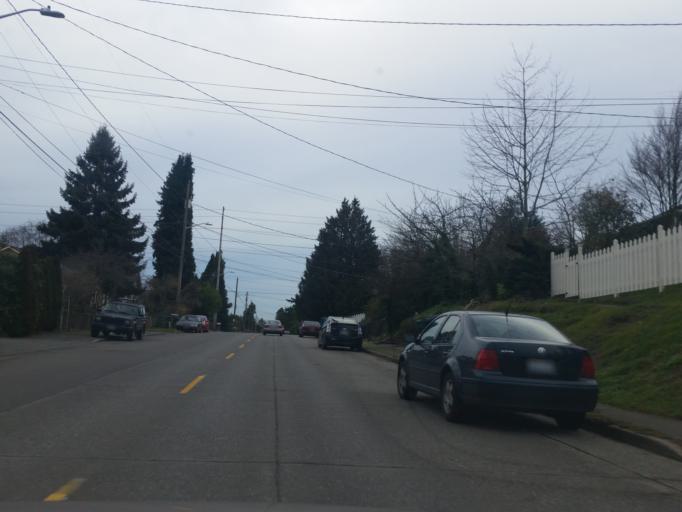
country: US
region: Washington
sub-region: King County
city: Shoreline
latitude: 47.6967
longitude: -122.3607
